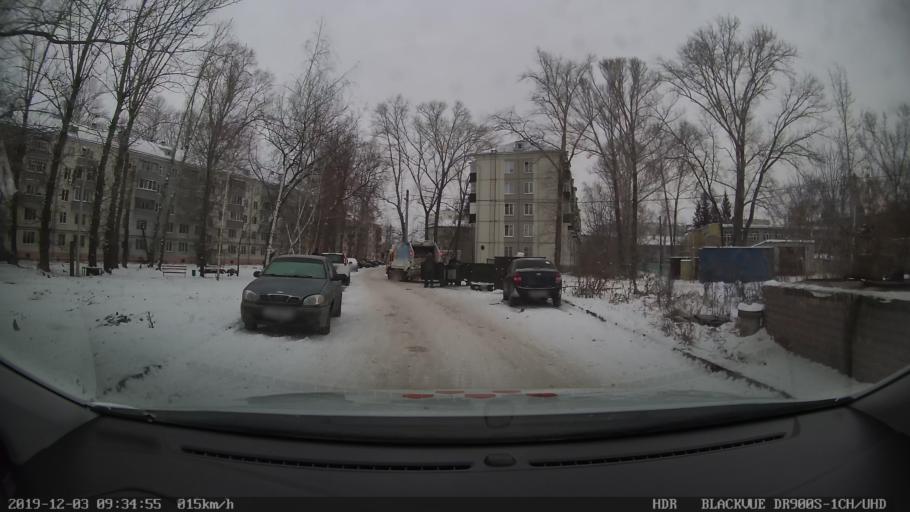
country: RU
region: Tatarstan
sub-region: Gorod Kazan'
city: Kazan
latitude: 55.7744
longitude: 49.1106
